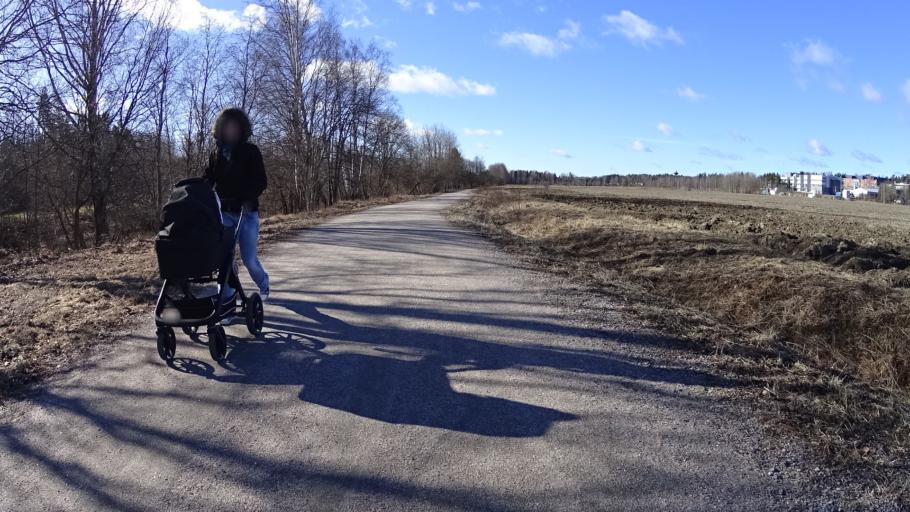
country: FI
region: Uusimaa
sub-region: Helsinki
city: Teekkarikylae
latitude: 60.2856
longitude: 24.8859
